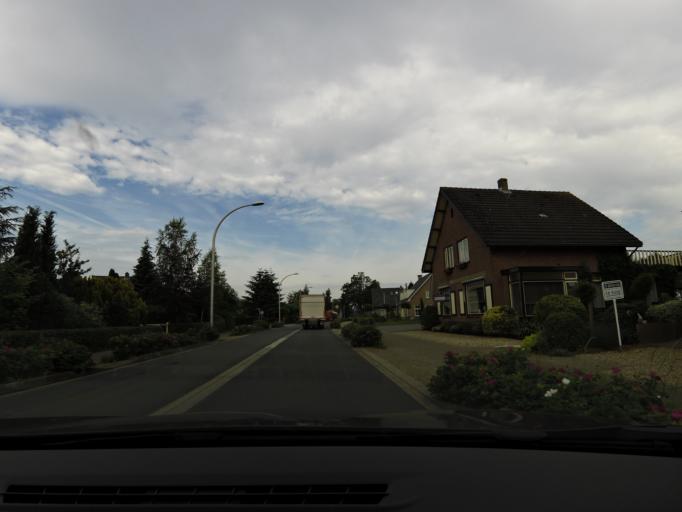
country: NL
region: Gelderland
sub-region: Gemeente Apeldoorn
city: Loenen
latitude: 52.1094
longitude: 6.0305
